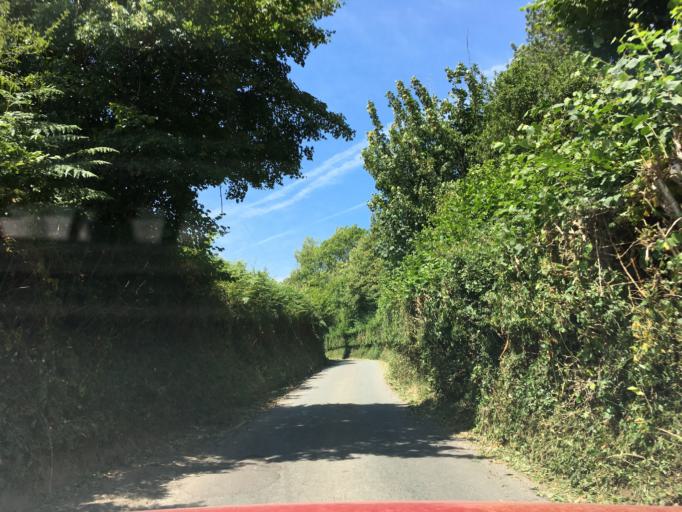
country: GB
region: Wales
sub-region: Caerphilly County Borough
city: Machen
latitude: 51.5512
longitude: -3.1426
